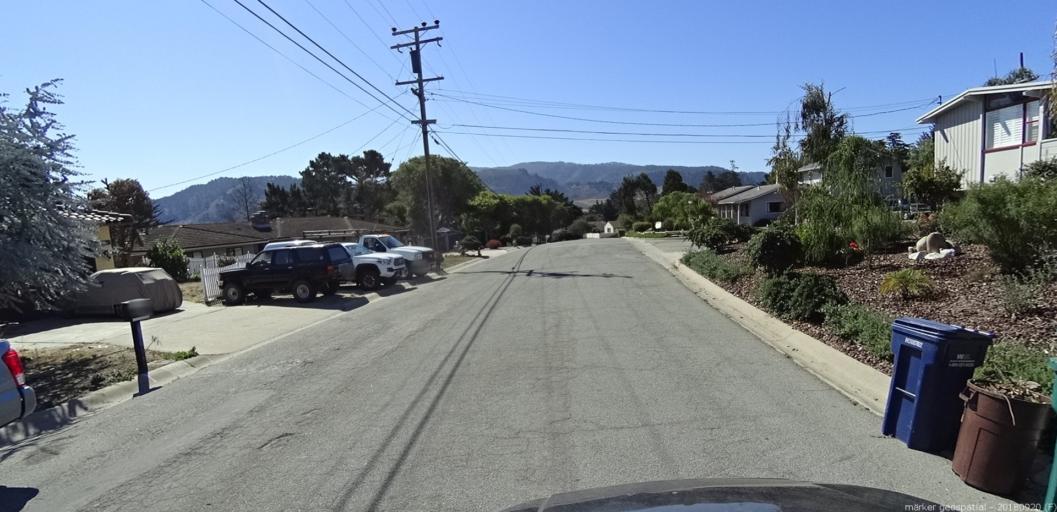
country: US
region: California
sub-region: Monterey County
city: Carmel-by-the-Sea
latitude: 36.5473
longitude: -121.9084
